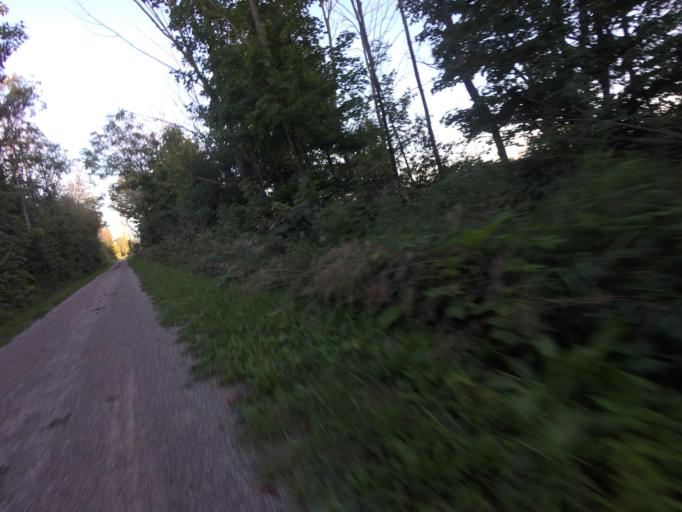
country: CA
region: Ontario
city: Goderich
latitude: 43.7579
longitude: -81.6849
